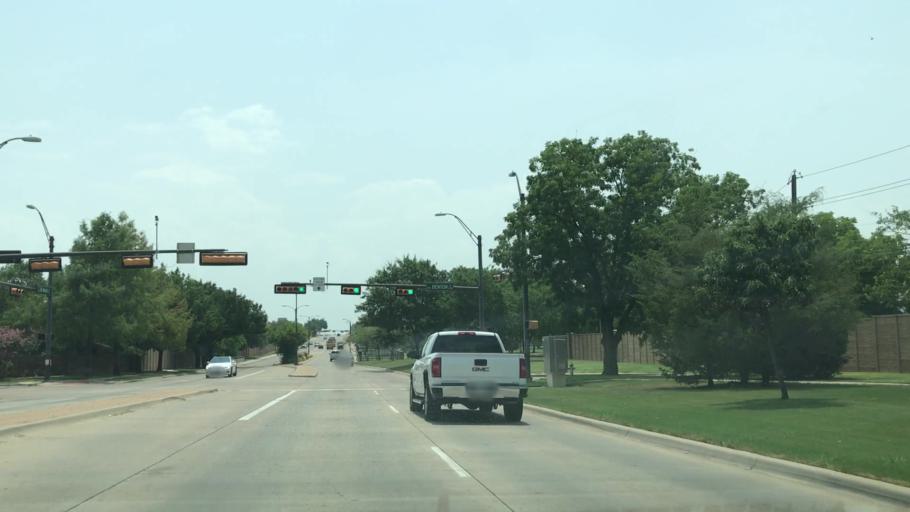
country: US
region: Texas
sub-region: Tarrant County
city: Euless
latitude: 32.8474
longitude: -97.0827
